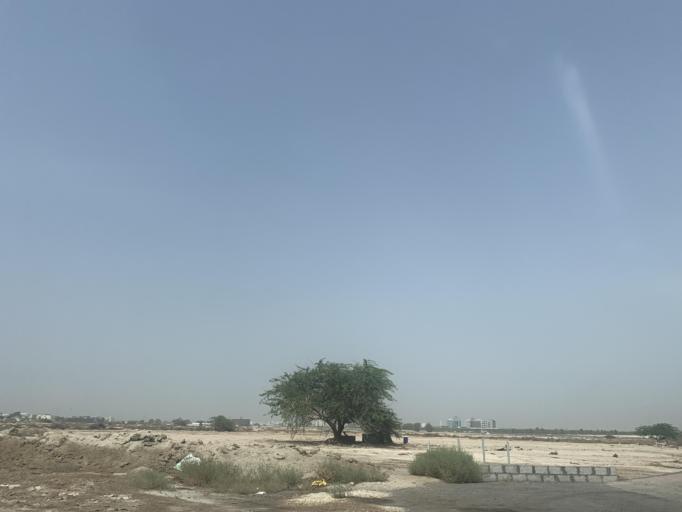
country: BH
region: Northern
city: Madinat `Isa
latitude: 26.1870
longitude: 50.4945
